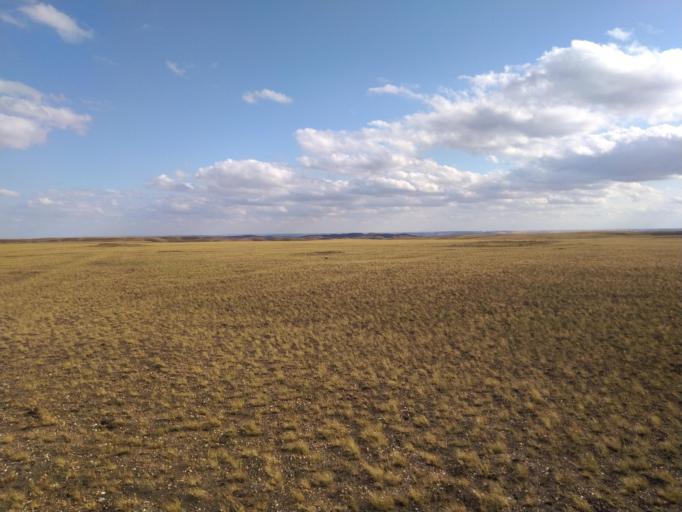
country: RU
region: Orenburg
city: Mednogorsk
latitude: 51.2106
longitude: 57.8342
